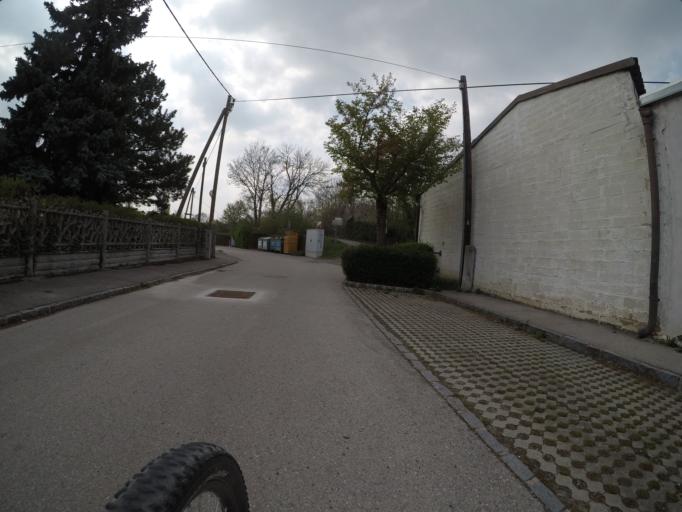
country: AT
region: Lower Austria
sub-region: Politischer Bezirk Baden
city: Pfaffstatten
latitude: 47.9997
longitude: 16.2598
